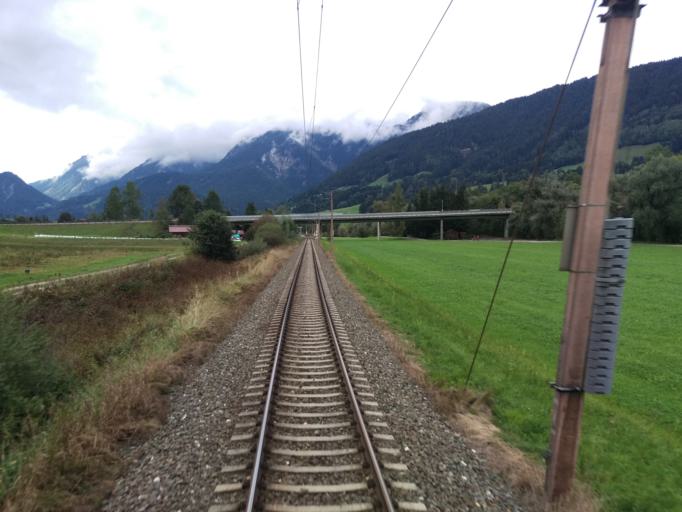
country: AT
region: Styria
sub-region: Politischer Bezirk Liezen
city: Aich
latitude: 47.4186
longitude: 13.8251
